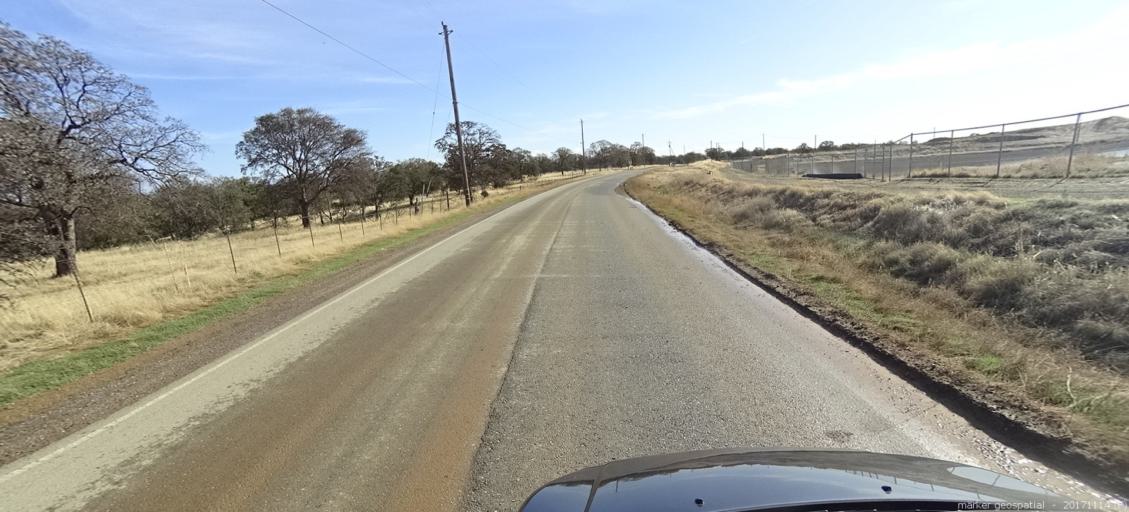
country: US
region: California
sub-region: Shasta County
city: Anderson
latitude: 40.4172
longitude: -122.3525
